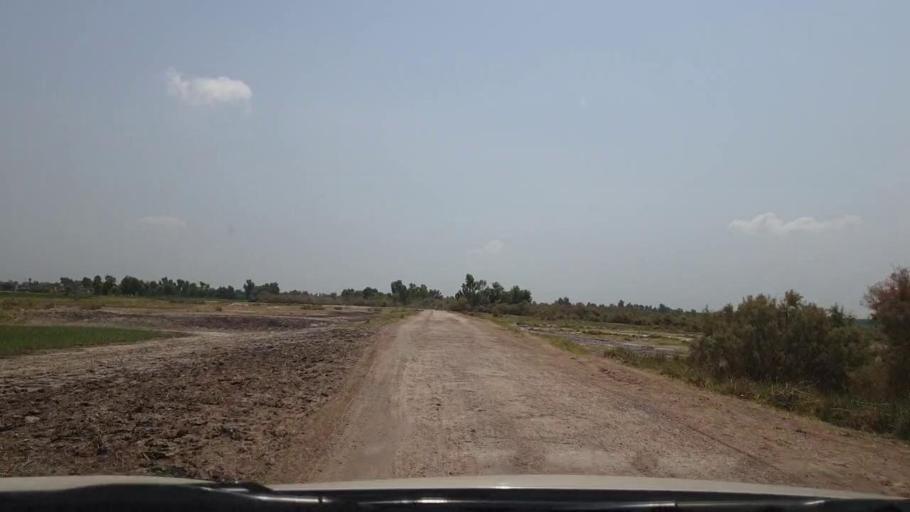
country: PK
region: Sindh
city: New Badah
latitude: 27.2988
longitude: 68.0645
